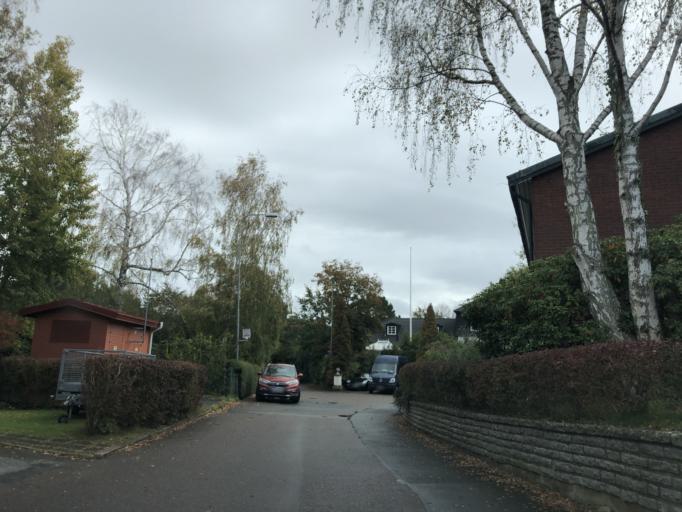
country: SE
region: Vaestra Goetaland
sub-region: Goteborg
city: Majorna
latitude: 57.6709
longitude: 11.8584
